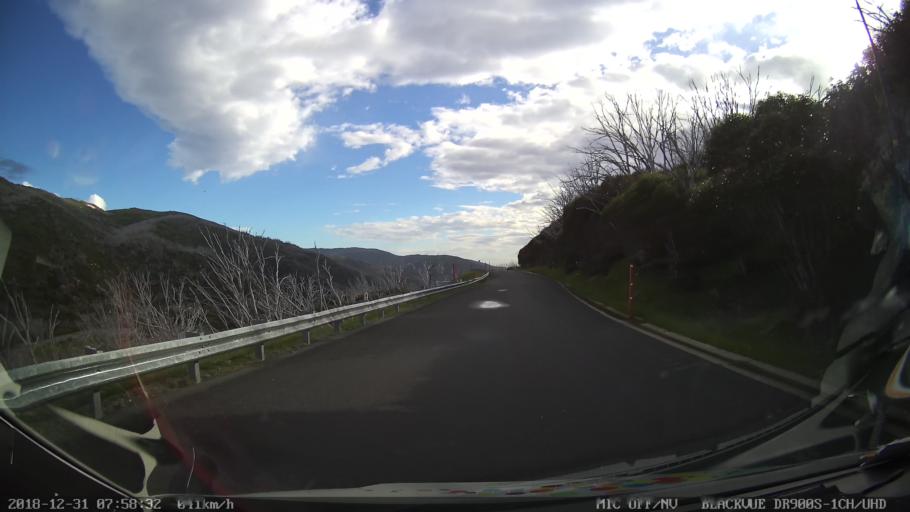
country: AU
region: New South Wales
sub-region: Snowy River
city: Jindabyne
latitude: -36.3744
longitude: 148.3798
